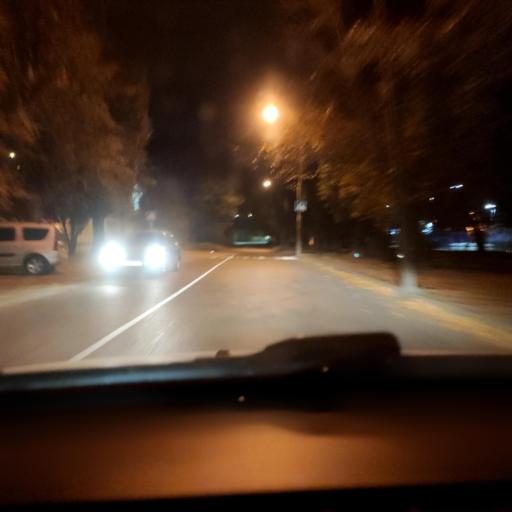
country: RU
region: Voronezj
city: Voronezh
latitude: 51.6830
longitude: 39.1952
